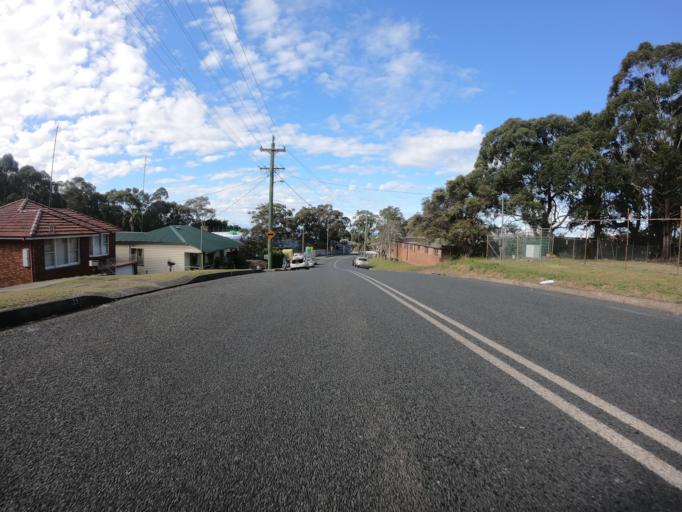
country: AU
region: New South Wales
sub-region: Wollongong
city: Bulli
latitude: -34.3357
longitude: 150.9065
